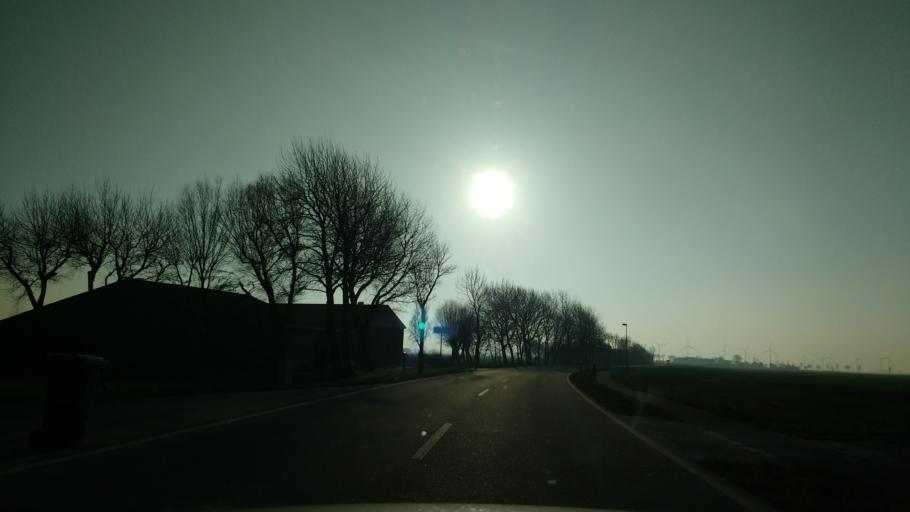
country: DE
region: Schleswig-Holstein
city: Helse
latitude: 53.9933
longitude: 8.9961
